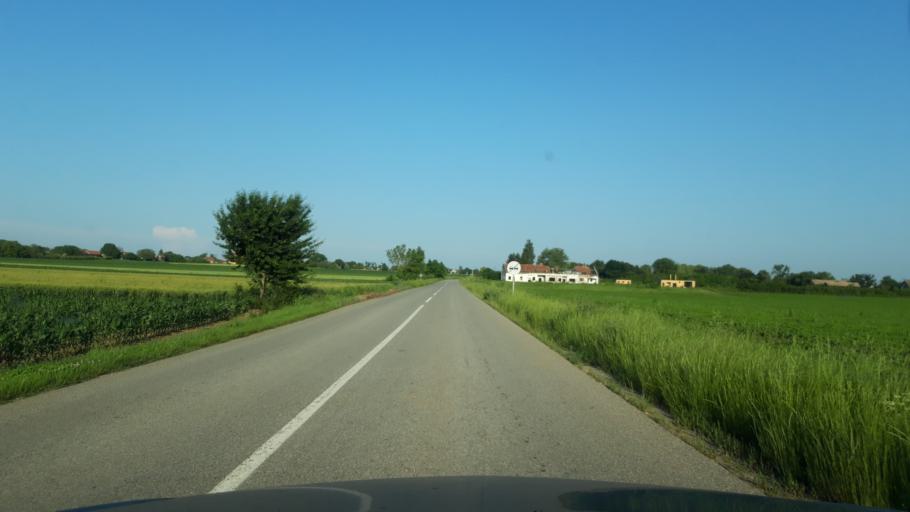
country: HR
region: Vukovarsko-Srijemska
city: Ilok
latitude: 45.1059
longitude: 19.4941
